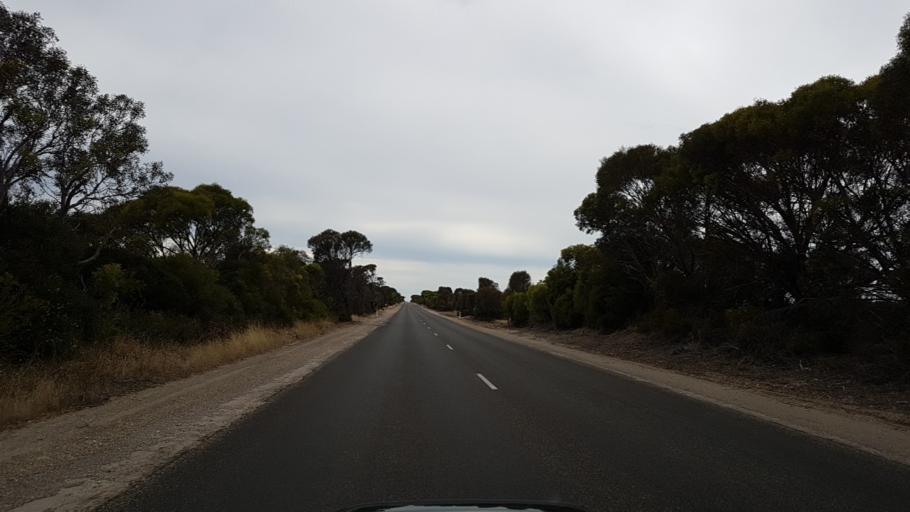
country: AU
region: South Australia
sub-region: Yorke Peninsula
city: Honiton
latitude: -34.9883
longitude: 137.1371
